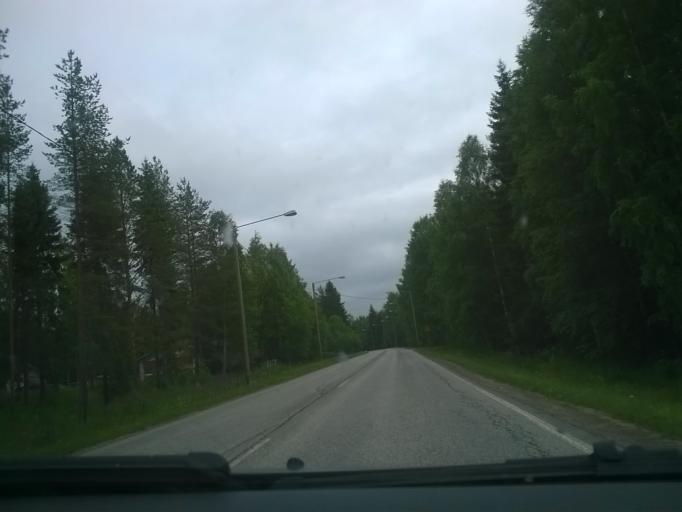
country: FI
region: Kainuu
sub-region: Kehys-Kainuu
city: Kuhmo
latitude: 64.1333
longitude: 29.4607
